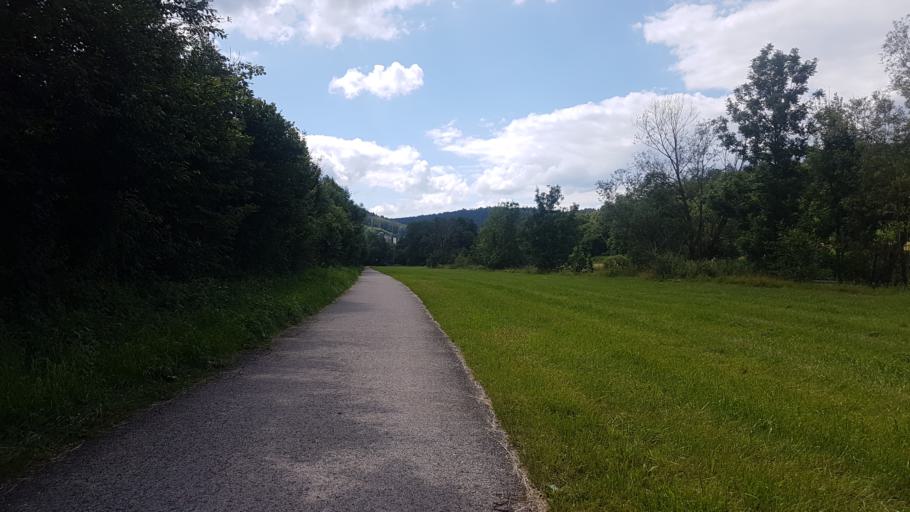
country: DE
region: Bavaria
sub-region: Regierungsbezirk Mittelfranken
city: Pappenheim
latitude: 48.9226
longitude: 10.9774
